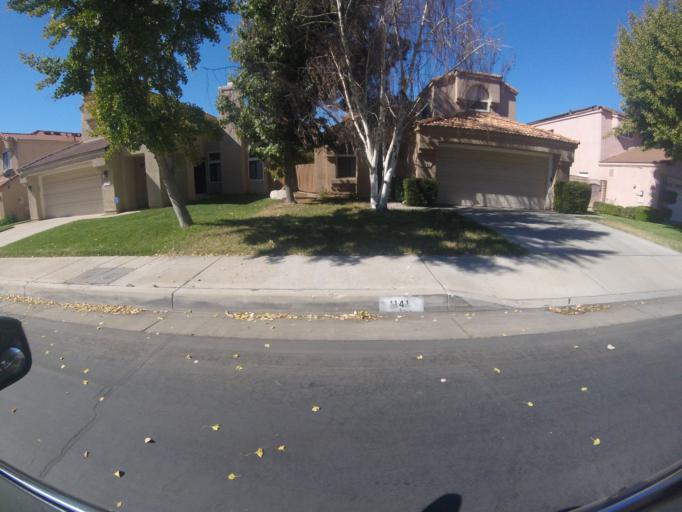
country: US
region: California
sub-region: San Bernardino County
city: Mentone
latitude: 34.0676
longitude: -117.1444
